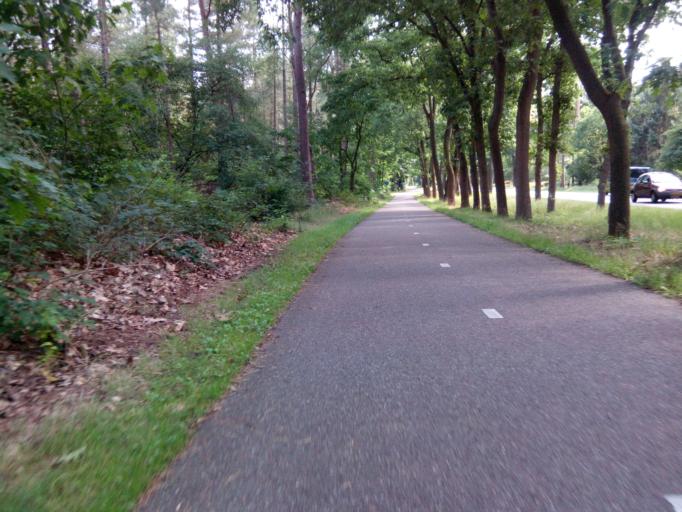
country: NL
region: Utrecht
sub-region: Gemeente Utrechtse Heuvelrug
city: Maarn
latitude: 52.0762
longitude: 5.3597
